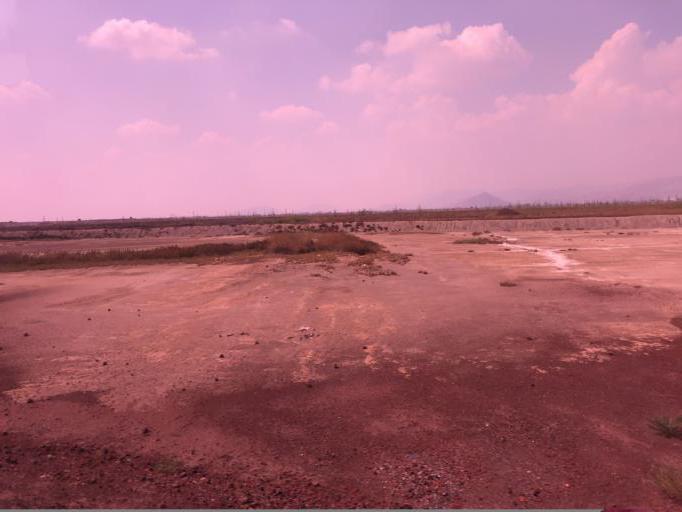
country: MX
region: Mexico
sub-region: Atenco
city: Colonia el Salado
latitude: 19.5477
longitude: -98.9848
